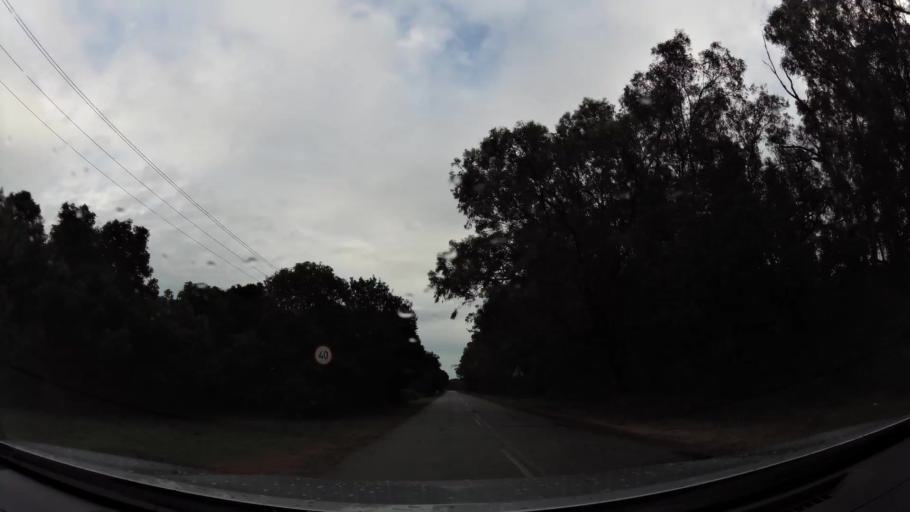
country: ZA
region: Eastern Cape
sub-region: Nelson Mandela Bay Metropolitan Municipality
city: Port Elizabeth
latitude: -34.0160
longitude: 25.5130
